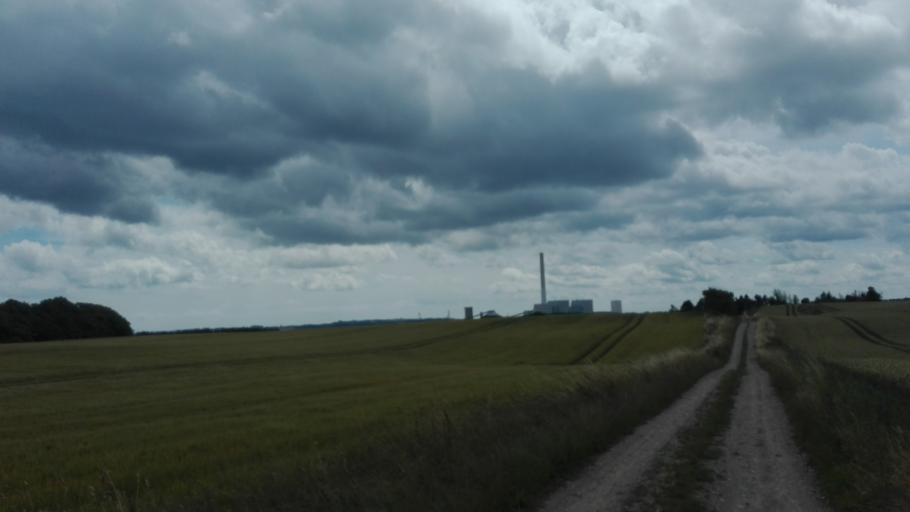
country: DK
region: Central Jutland
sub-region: Arhus Kommune
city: Logten
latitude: 56.2694
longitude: 10.3400
